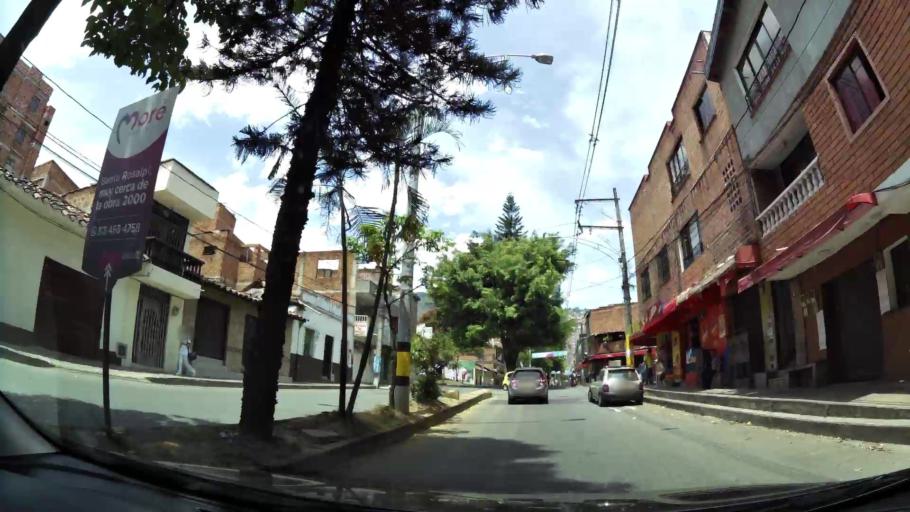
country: CO
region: Antioquia
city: Bello
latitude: 6.3400
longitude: -75.5633
